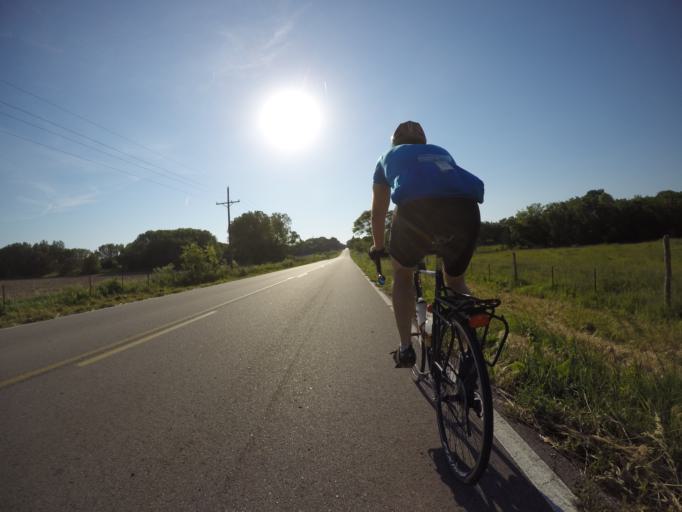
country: US
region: Nebraska
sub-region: Gage County
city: Wymore
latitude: 40.0883
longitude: -96.4896
